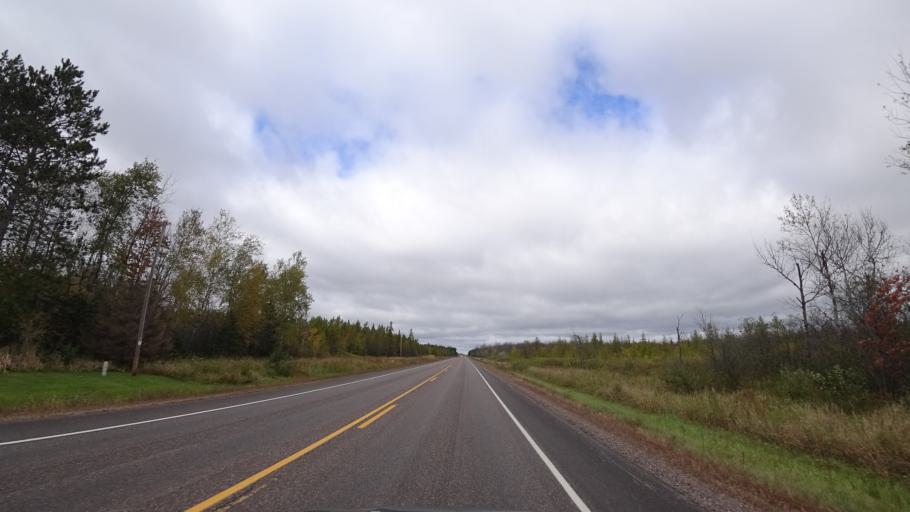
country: US
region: Wisconsin
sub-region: Rusk County
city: Ladysmith
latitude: 45.4057
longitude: -91.1103
